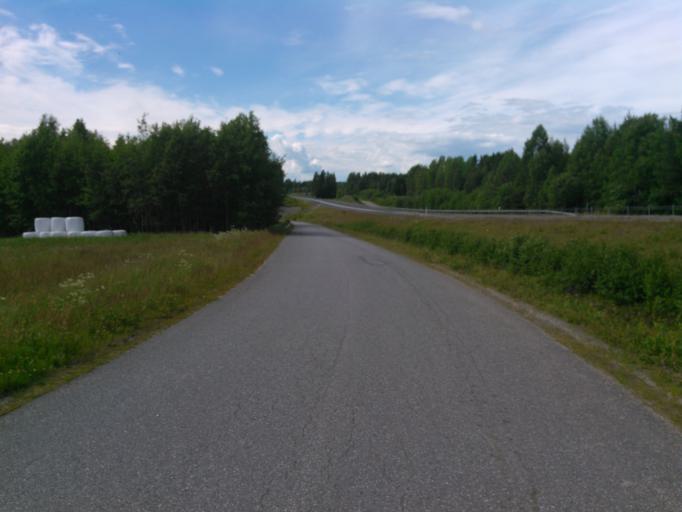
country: SE
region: Vaesterbotten
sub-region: Vannas Kommun
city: Vannasby
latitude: 63.8928
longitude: 19.9810
